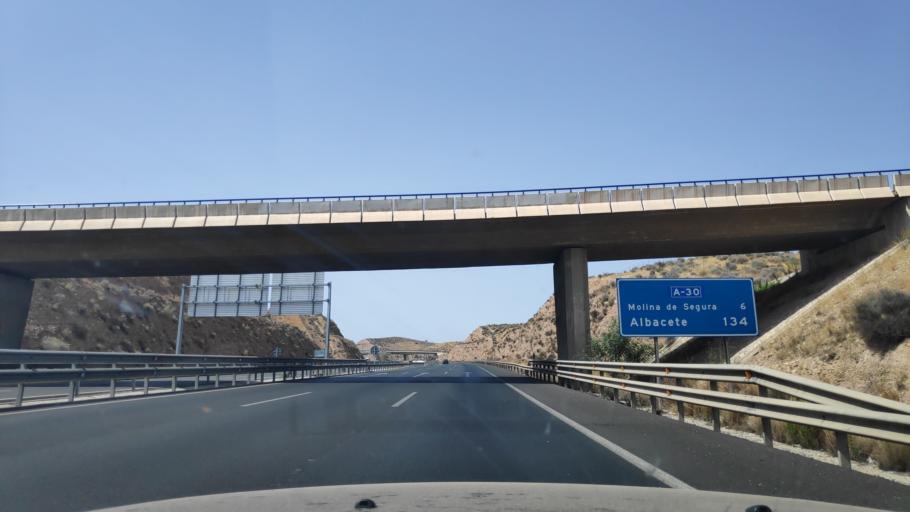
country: ES
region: Murcia
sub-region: Murcia
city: Molina de Segura
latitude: 38.0368
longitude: -1.1604
